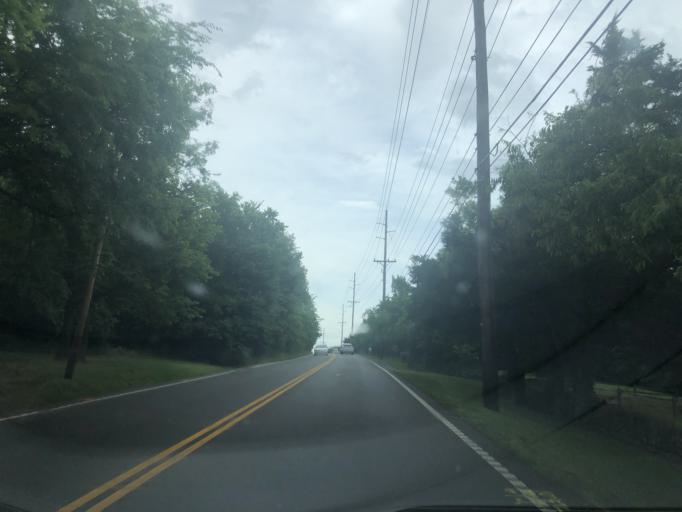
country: US
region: Tennessee
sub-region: Davidson County
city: Forest Hills
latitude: 36.0453
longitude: -86.8535
